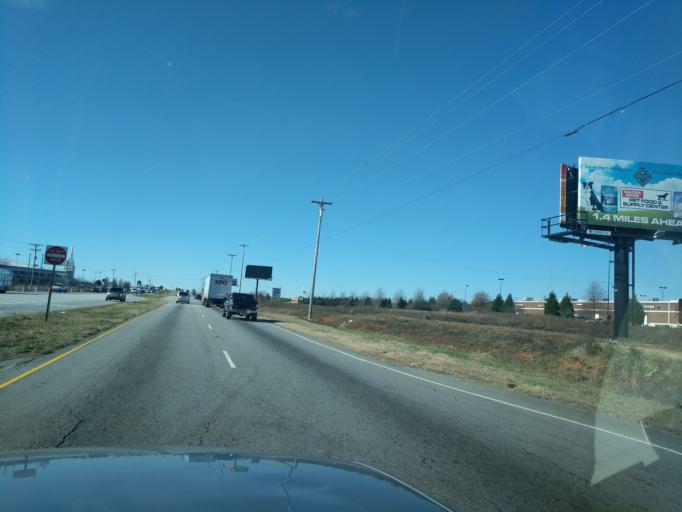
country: US
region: South Carolina
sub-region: Pickens County
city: Easley
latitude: 34.8262
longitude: -82.5443
